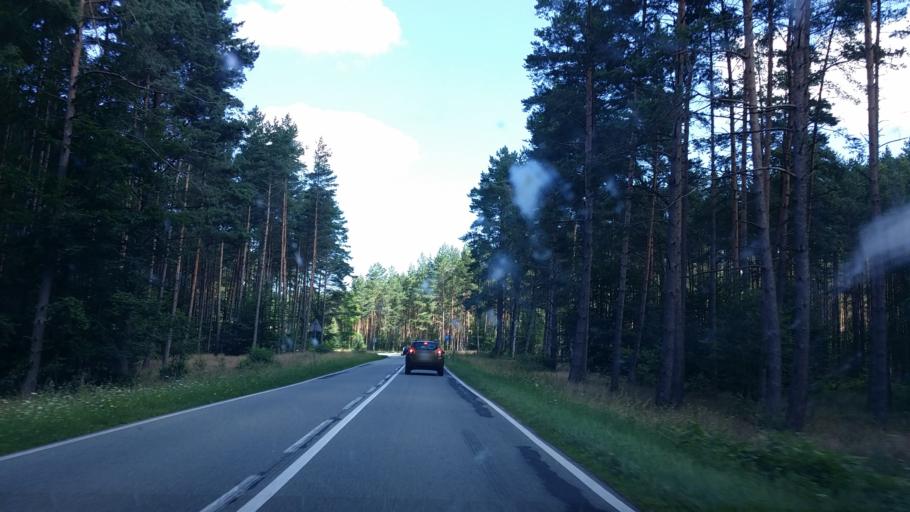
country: PL
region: West Pomeranian Voivodeship
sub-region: Powiat drawski
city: Drawsko Pomorskie
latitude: 53.4295
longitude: 15.8269
